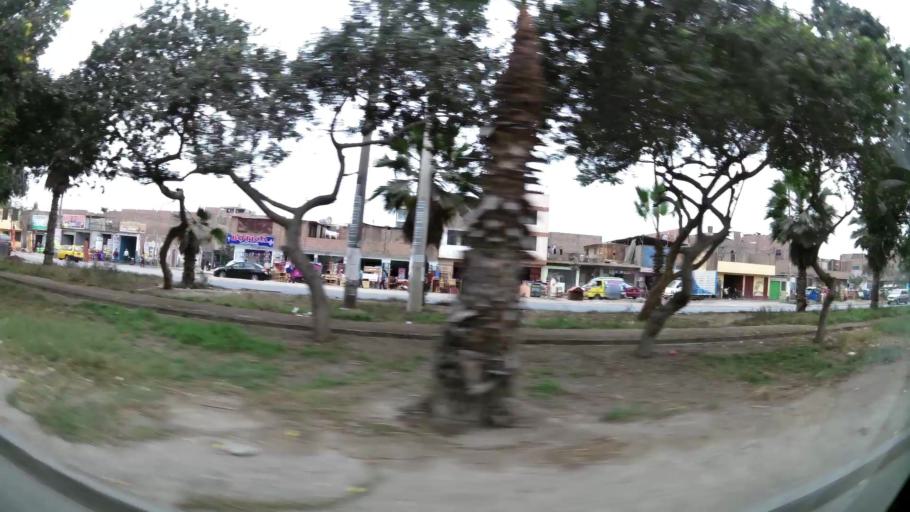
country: PE
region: Lima
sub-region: Lima
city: Urb. Santo Domingo
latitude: -11.9232
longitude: -77.0515
